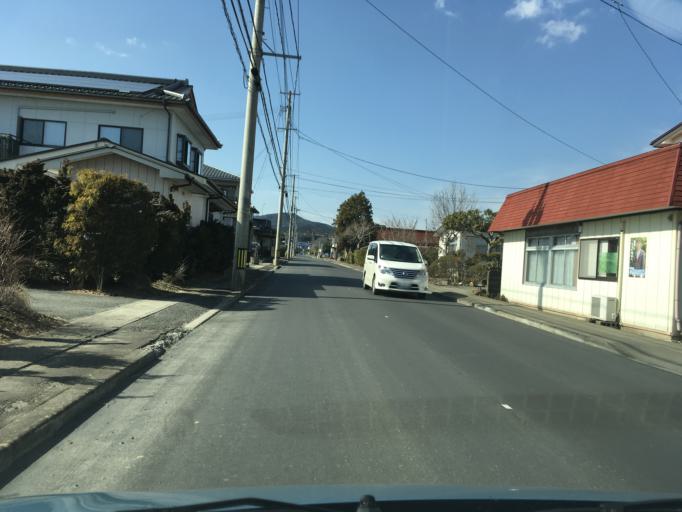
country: JP
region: Iwate
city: Ofunato
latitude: 38.8337
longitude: 141.5819
